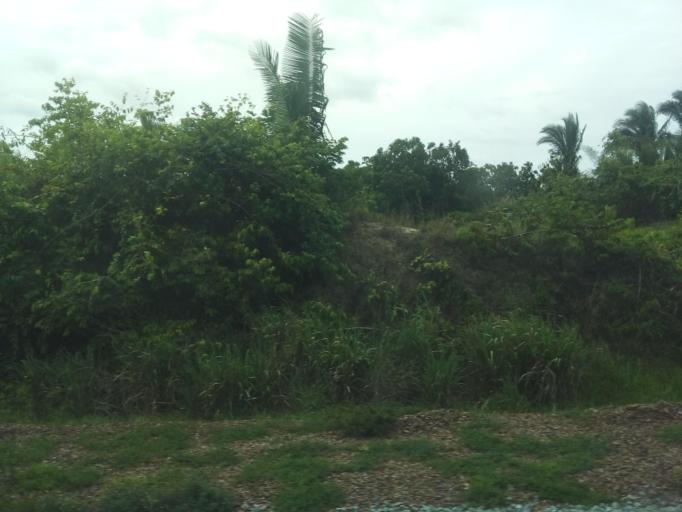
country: BR
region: Maranhao
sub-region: Santa Ines
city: Santa Ines
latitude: -3.7018
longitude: -45.9981
